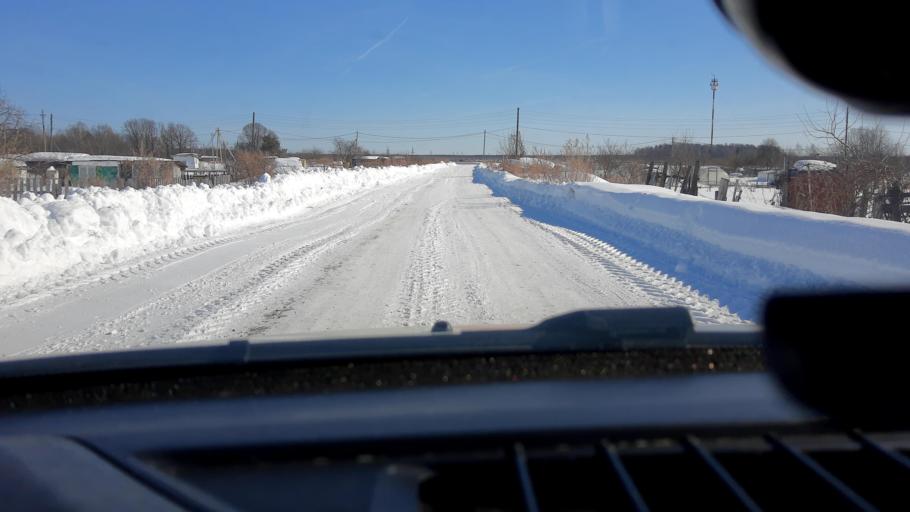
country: RU
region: Nizjnij Novgorod
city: Volodarsk
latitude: 56.2459
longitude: 43.1878
